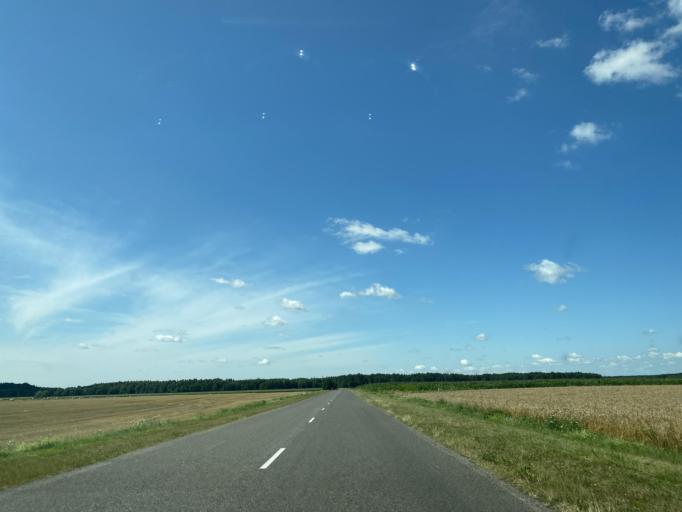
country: BY
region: Brest
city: Ivanava
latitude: 52.2304
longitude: 25.6466
